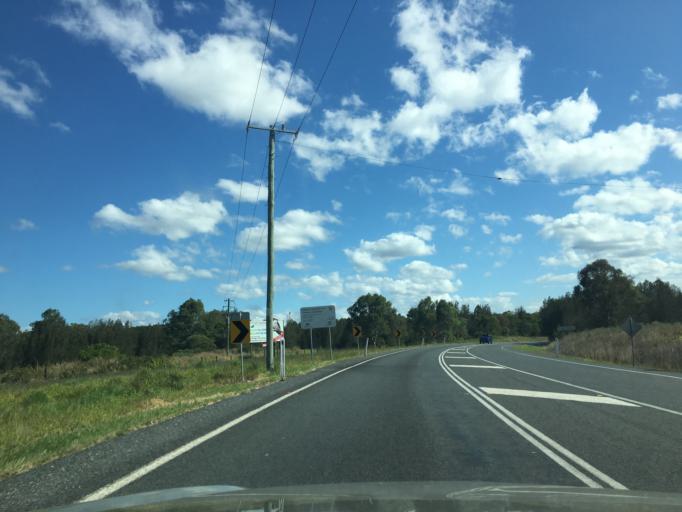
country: AU
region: Queensland
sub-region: Logan
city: Logan Reserve
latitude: -27.7508
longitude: 153.1252
